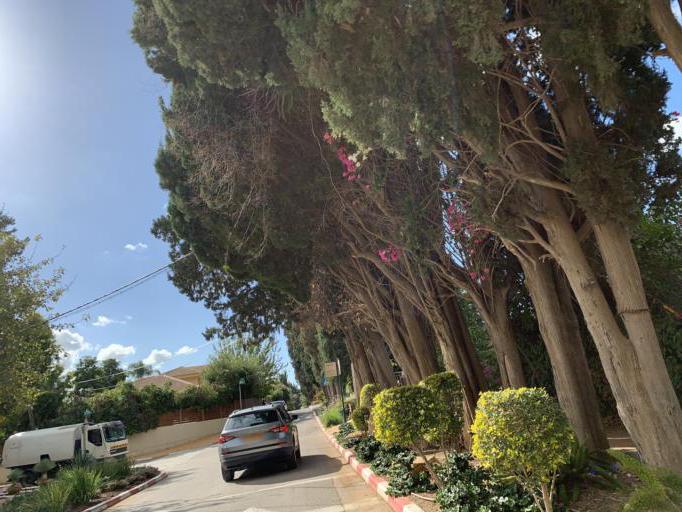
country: IL
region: Central District
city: Hod HaSharon
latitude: 32.1689
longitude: 34.8867
